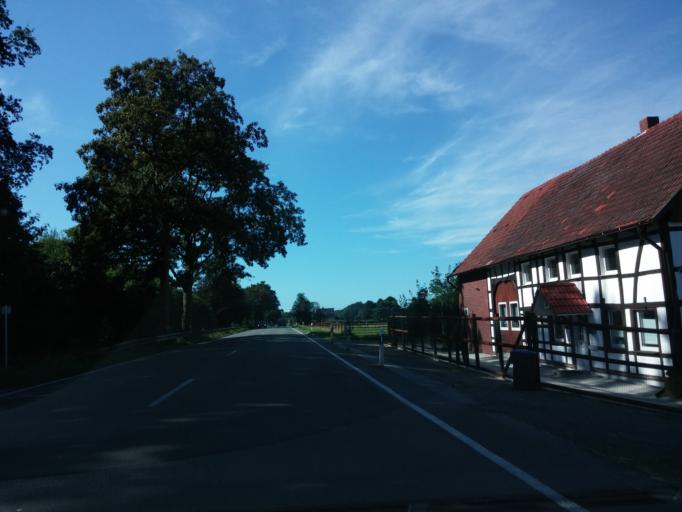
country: DE
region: North Rhine-Westphalia
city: Dorsten
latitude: 51.6275
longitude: 7.0082
